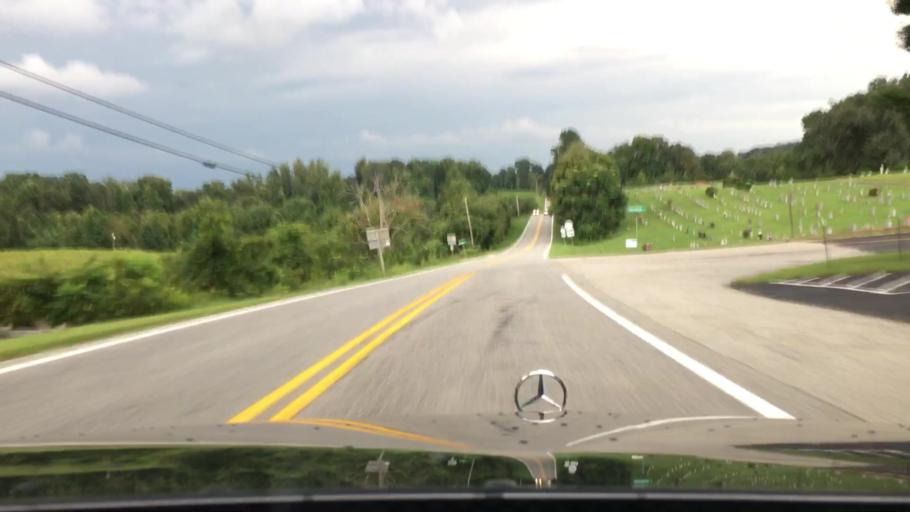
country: US
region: Virginia
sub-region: Nelson County
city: Lovingston
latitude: 37.7836
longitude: -78.9782
